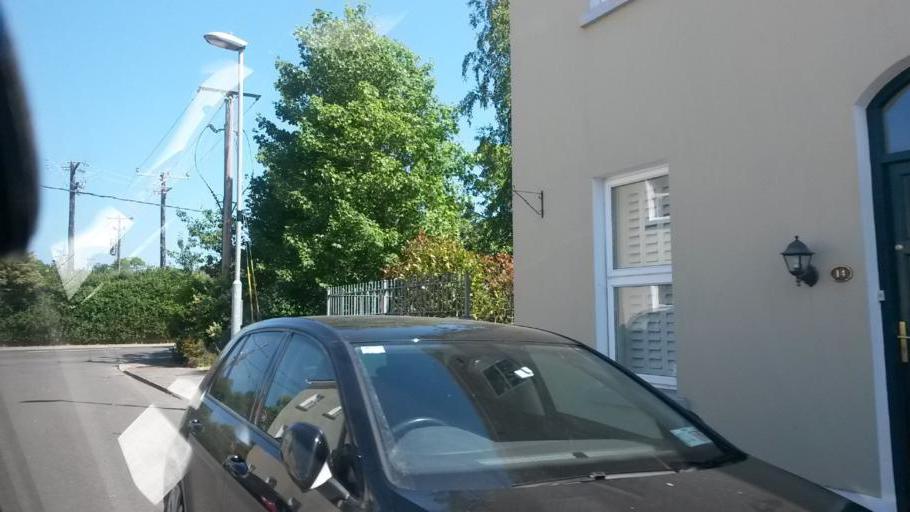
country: IE
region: Leinster
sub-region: An Mhi
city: Stamullin
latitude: 53.5841
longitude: -6.2888
